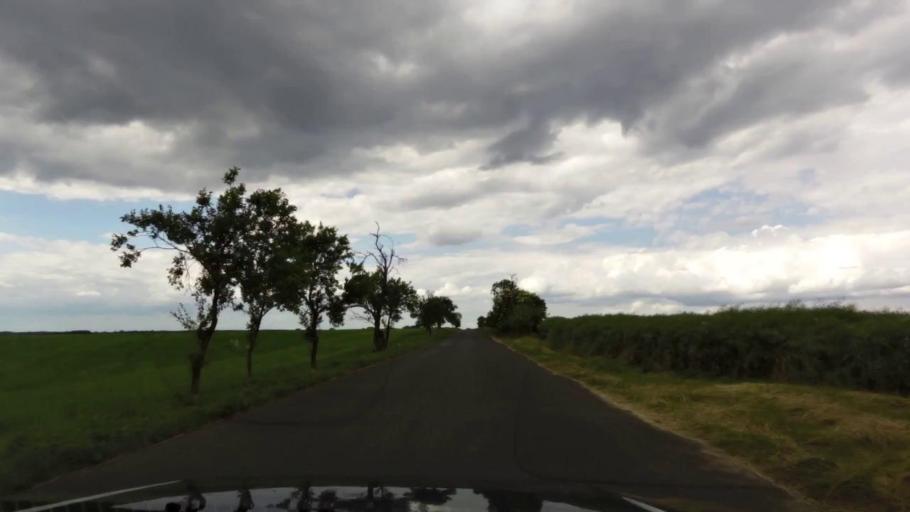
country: PL
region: West Pomeranian Voivodeship
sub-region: Powiat mysliborski
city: Mysliborz
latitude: 52.9799
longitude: 14.7846
